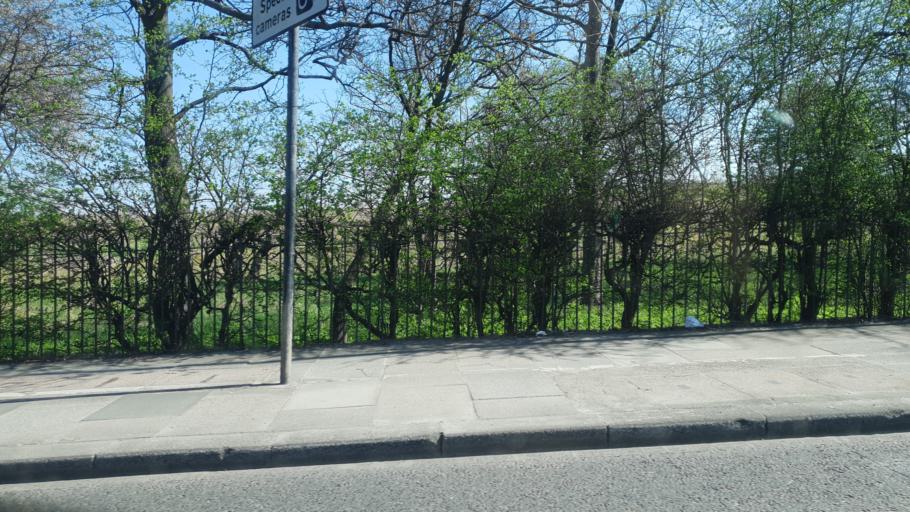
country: GB
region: England
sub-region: Middlesbrough
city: Middlesbrough
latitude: 54.5535
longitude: -1.2198
